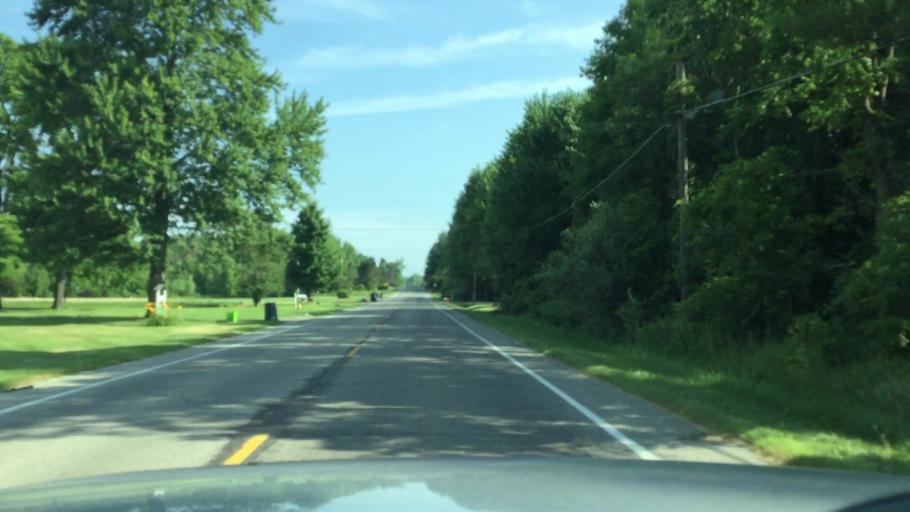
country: US
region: Michigan
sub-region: Genesee County
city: Flushing
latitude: 43.1118
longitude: -83.8728
